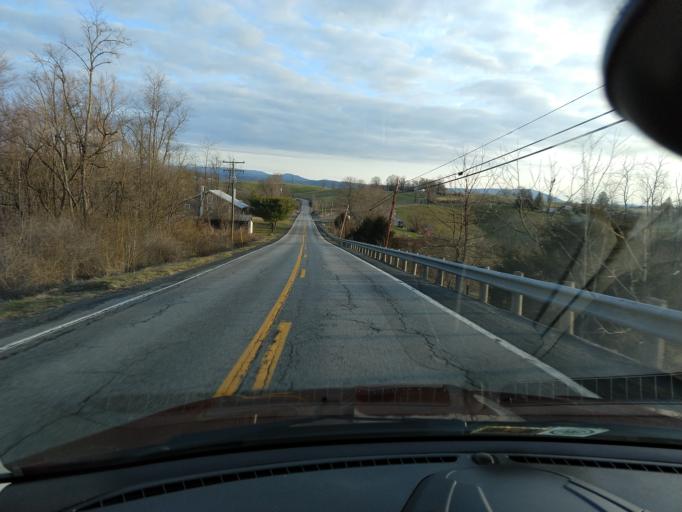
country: US
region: West Virginia
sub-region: Greenbrier County
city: Lewisburg
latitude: 37.9436
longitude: -80.3772
